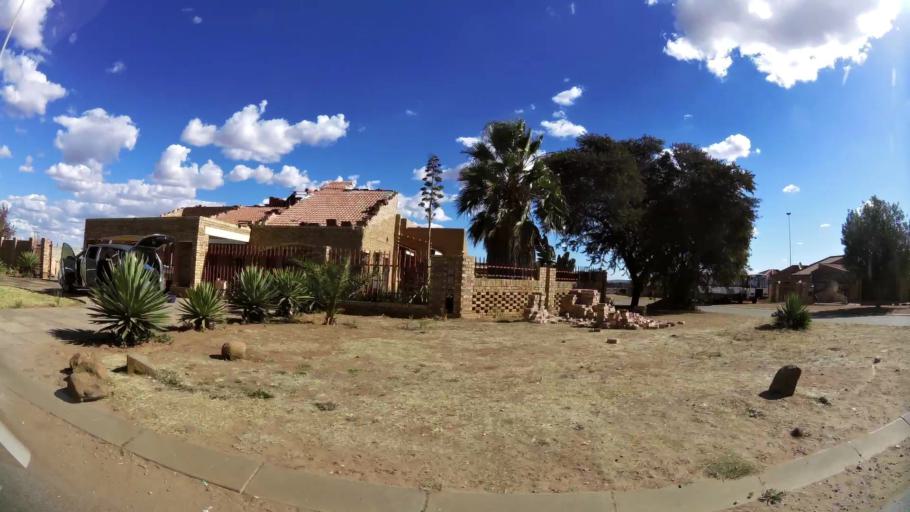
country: ZA
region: North-West
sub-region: Dr Kenneth Kaunda District Municipality
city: Klerksdorp
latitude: -26.8765
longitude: 26.5823
